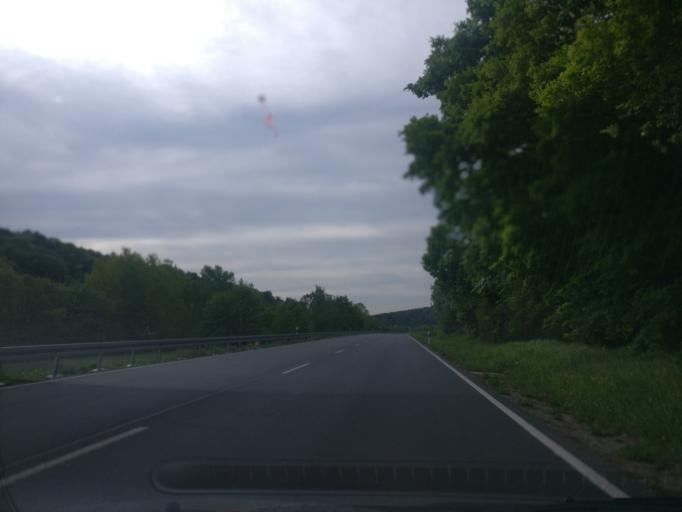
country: DE
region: Hesse
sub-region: Regierungsbezirk Kassel
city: Fuldatal
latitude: 51.3629
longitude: 9.5513
